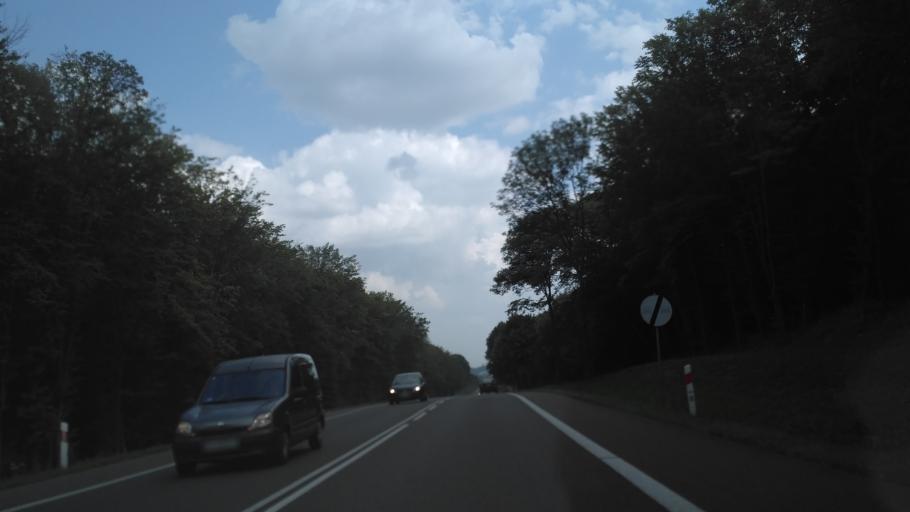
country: PL
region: Lublin Voivodeship
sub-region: Chelm
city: Chelm
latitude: 51.1533
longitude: 23.4159
